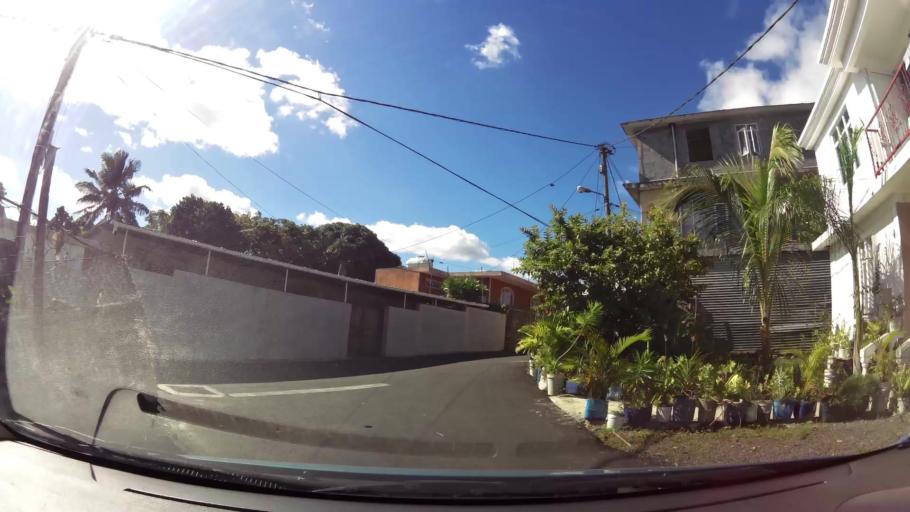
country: MU
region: Plaines Wilhems
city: Vacoas
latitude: -20.2823
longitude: 57.4780
